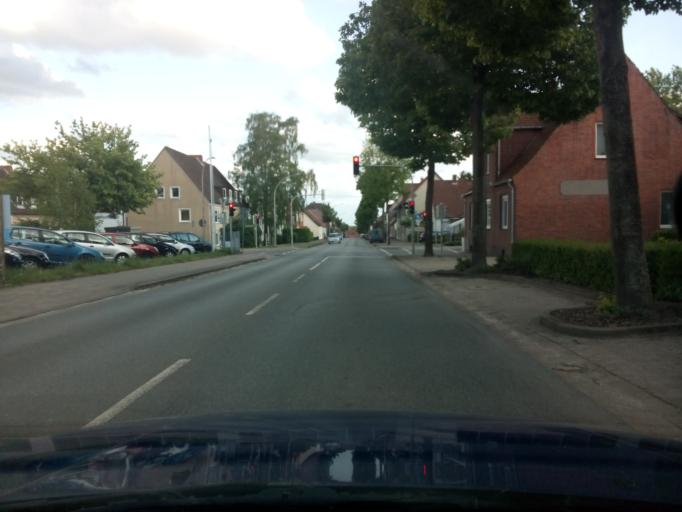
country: DE
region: Lower Saxony
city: Walsrode
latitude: 52.8681
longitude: 9.5854
